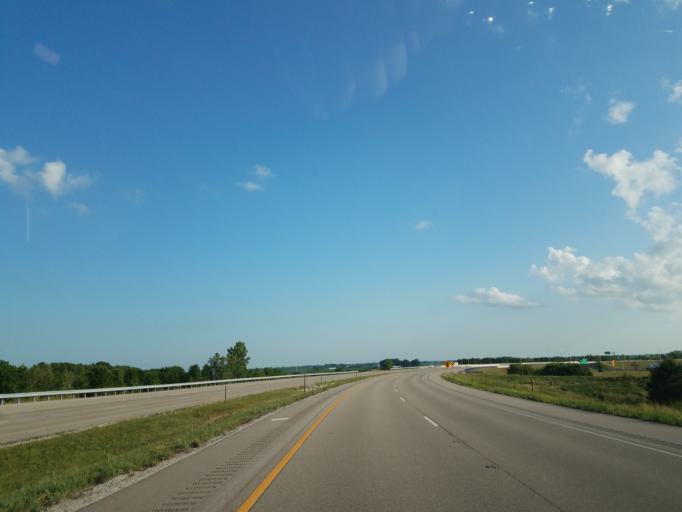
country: US
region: Illinois
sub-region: McLean County
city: Bloomington
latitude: 40.4447
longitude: -89.0166
